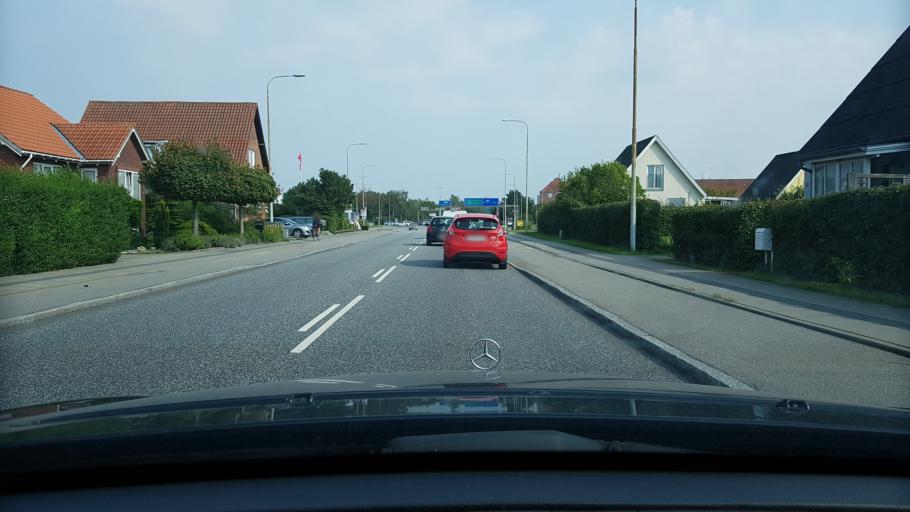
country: DK
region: North Denmark
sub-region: Alborg Kommune
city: Aalborg
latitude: 57.0701
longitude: 9.9433
